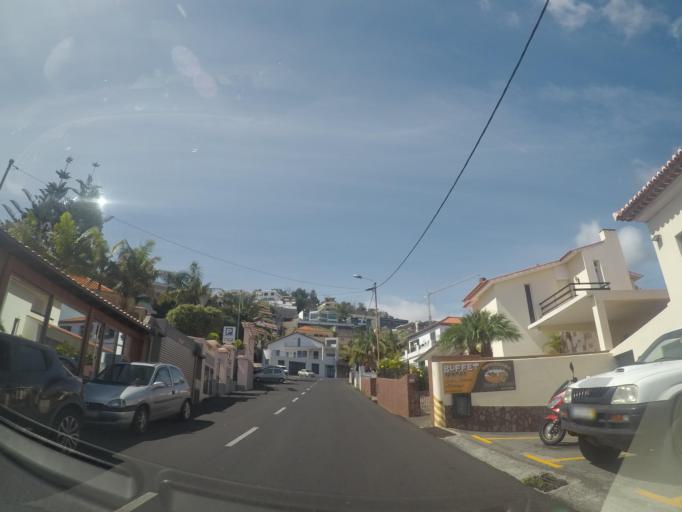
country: PT
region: Madeira
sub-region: Funchal
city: Funchal
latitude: 32.6496
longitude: -16.9320
